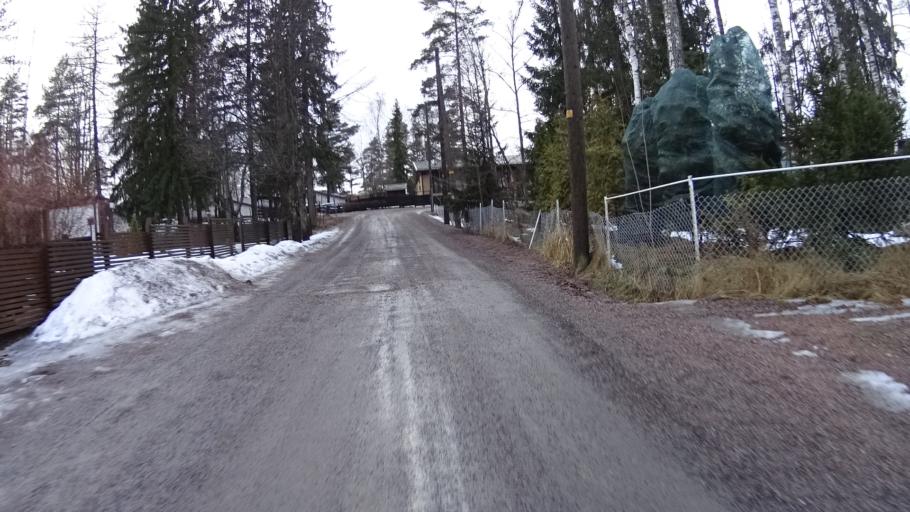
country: FI
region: Uusimaa
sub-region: Helsinki
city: Kilo
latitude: 60.2383
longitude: 24.7556
